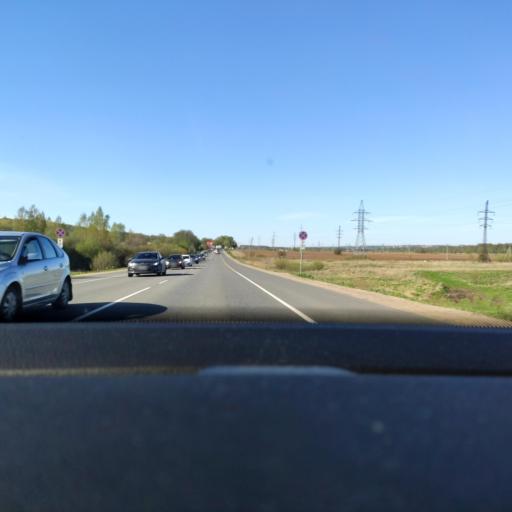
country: RU
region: Moskovskaya
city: Yakhroma
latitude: 56.3190
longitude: 37.4810
